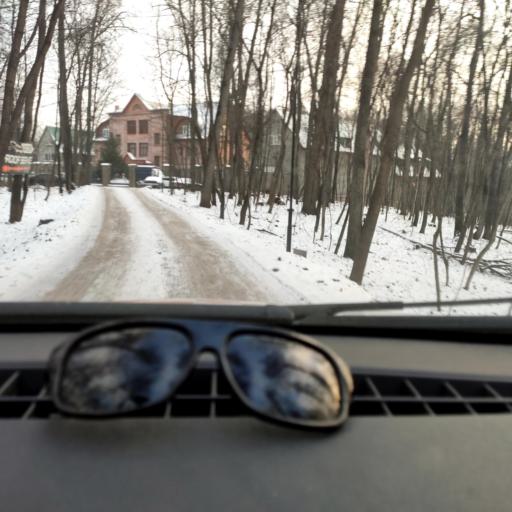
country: RU
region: Bashkortostan
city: Ufa
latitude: 54.7463
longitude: 56.0075
